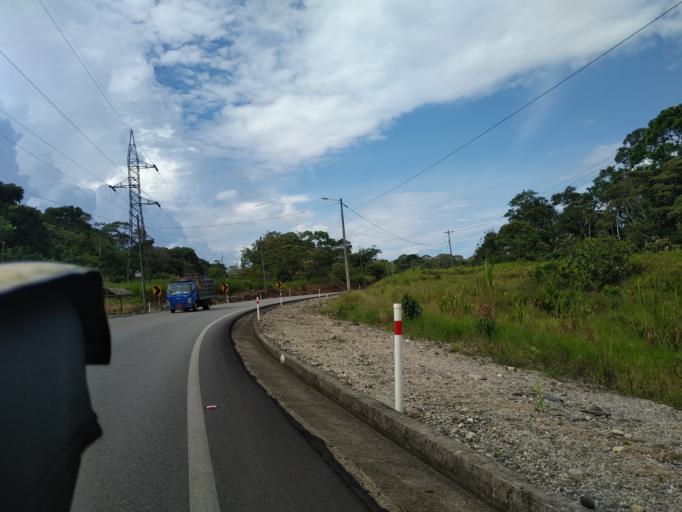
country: EC
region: Napo
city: Tena
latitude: -1.0923
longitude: -77.7923
